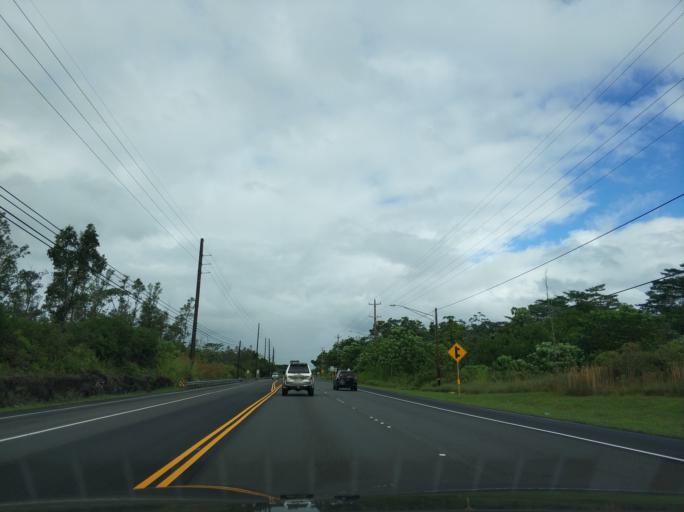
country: US
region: Hawaii
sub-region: Hawaii County
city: Kea'au
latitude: 19.6024
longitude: -155.0244
